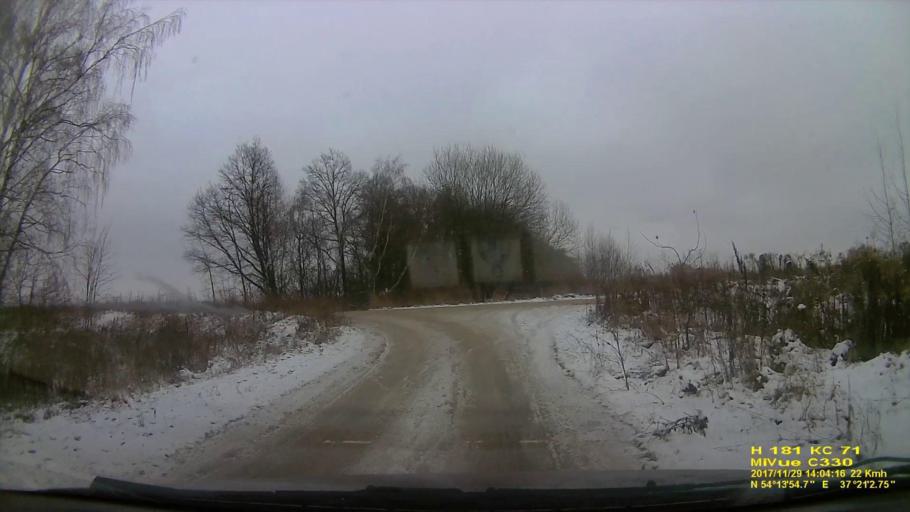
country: RU
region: Tula
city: Leninskiy
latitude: 54.2318
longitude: 37.3508
